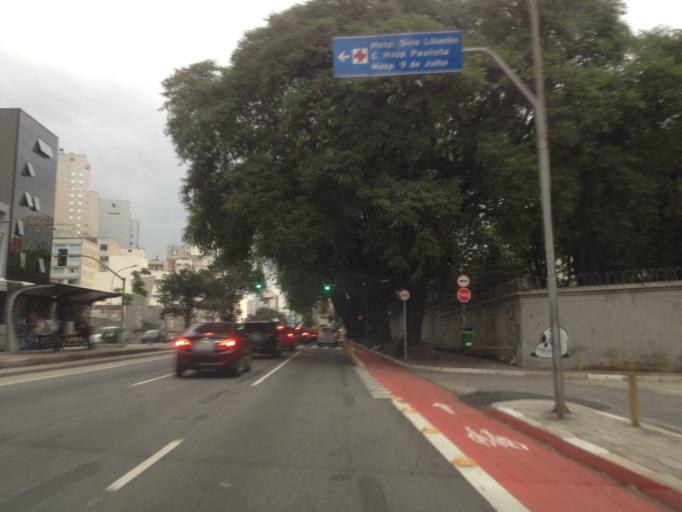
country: BR
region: Sao Paulo
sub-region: Sao Paulo
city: Sao Paulo
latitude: -23.5517
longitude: -46.6573
